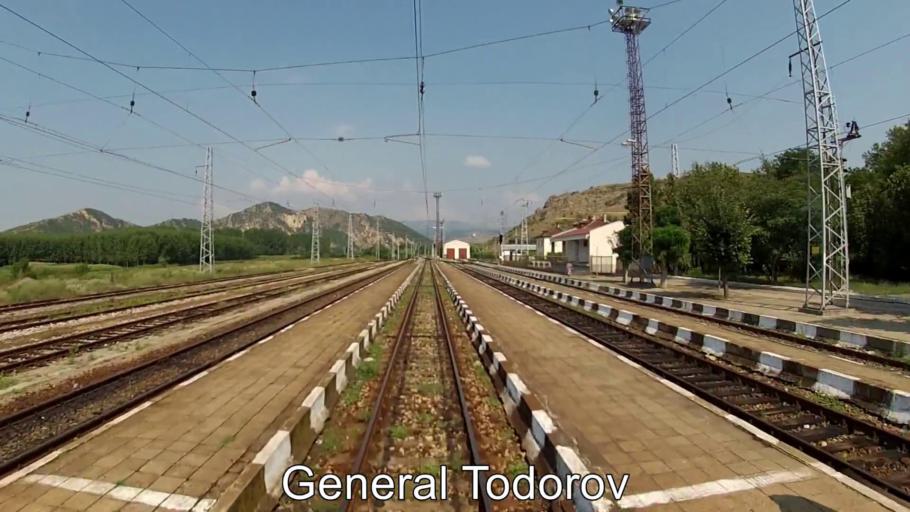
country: BG
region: Blagoevgrad
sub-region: Obshtina Petrich
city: Petrich
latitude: 41.4557
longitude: 23.2808
